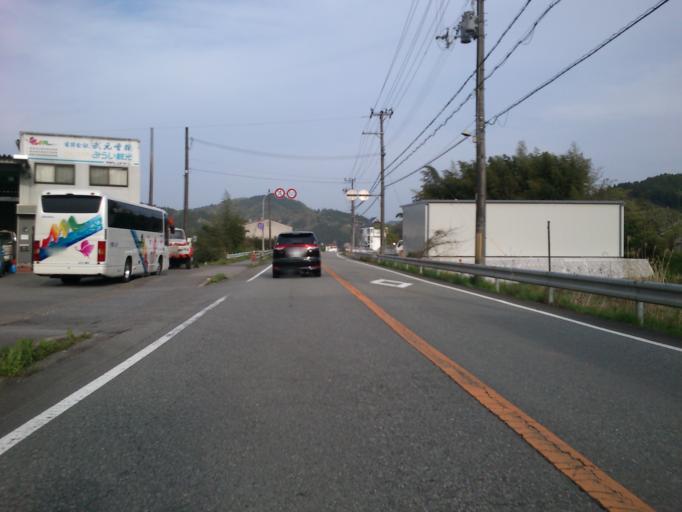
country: JP
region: Hyogo
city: Sasayama
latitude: 35.0803
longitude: 135.3240
